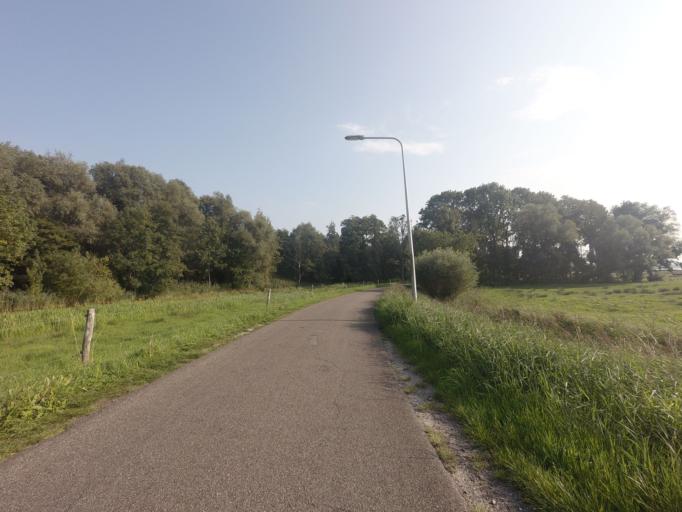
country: NL
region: Groningen
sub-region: Gemeente Haren
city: Haren
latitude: 53.1768
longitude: 6.5785
